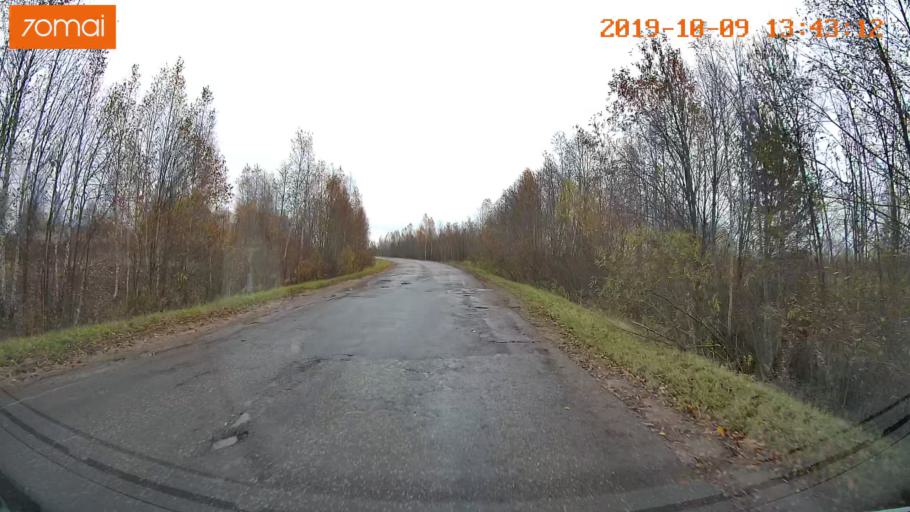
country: RU
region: Kostroma
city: Buy
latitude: 58.3566
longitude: 41.1976
